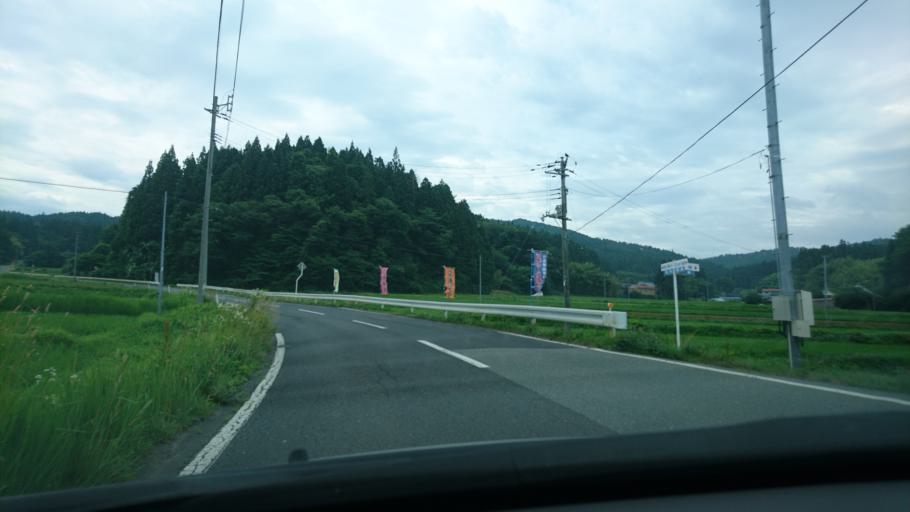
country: JP
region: Iwate
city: Ichinoseki
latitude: 38.8901
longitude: 141.4231
